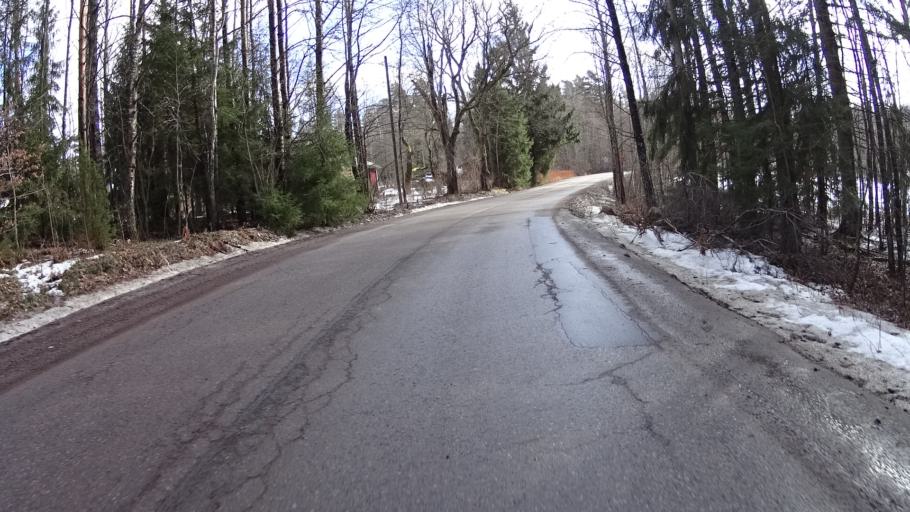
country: FI
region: Uusimaa
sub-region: Helsinki
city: Kauniainen
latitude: 60.2724
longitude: 24.6883
